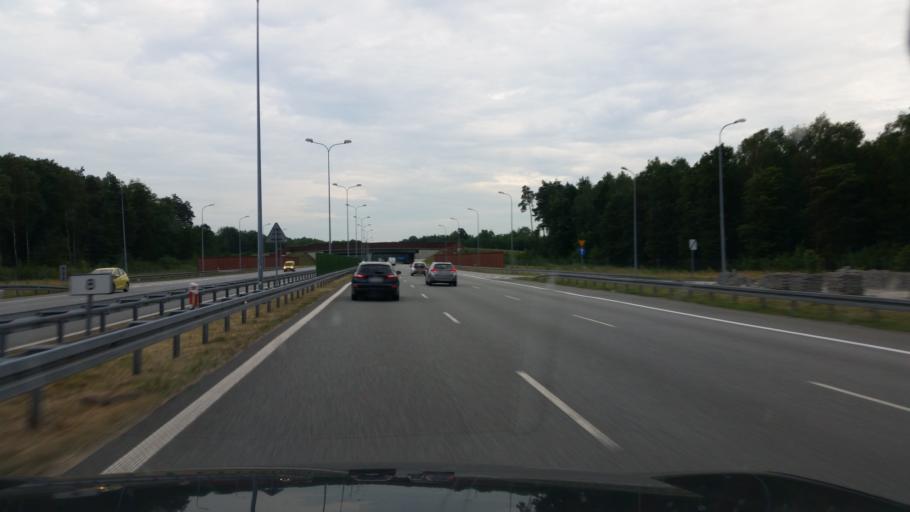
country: PL
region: Silesian Voivodeship
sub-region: Powiat gliwicki
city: Gieraltowice
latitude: 50.1960
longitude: 18.7022
